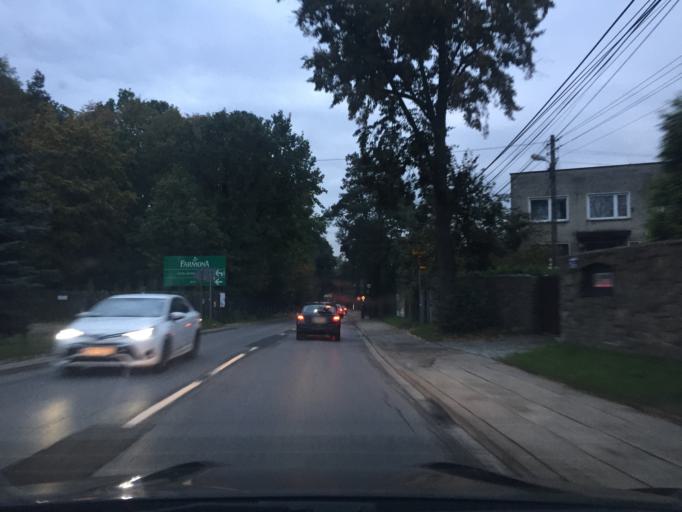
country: PL
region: Lesser Poland Voivodeship
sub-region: Powiat krakowski
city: Libertow
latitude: 50.0075
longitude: 19.9295
